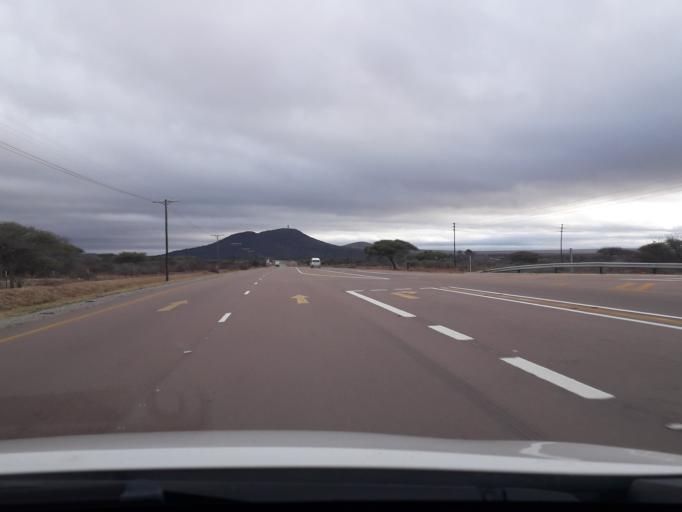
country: ZA
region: Limpopo
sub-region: Capricorn District Municipality
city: Polokwane
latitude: -23.7235
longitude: 29.5903
